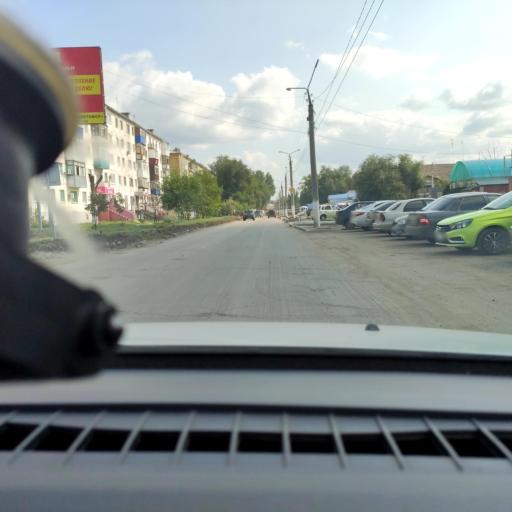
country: RU
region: Samara
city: Chapayevsk
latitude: 52.9551
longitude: 49.6896
